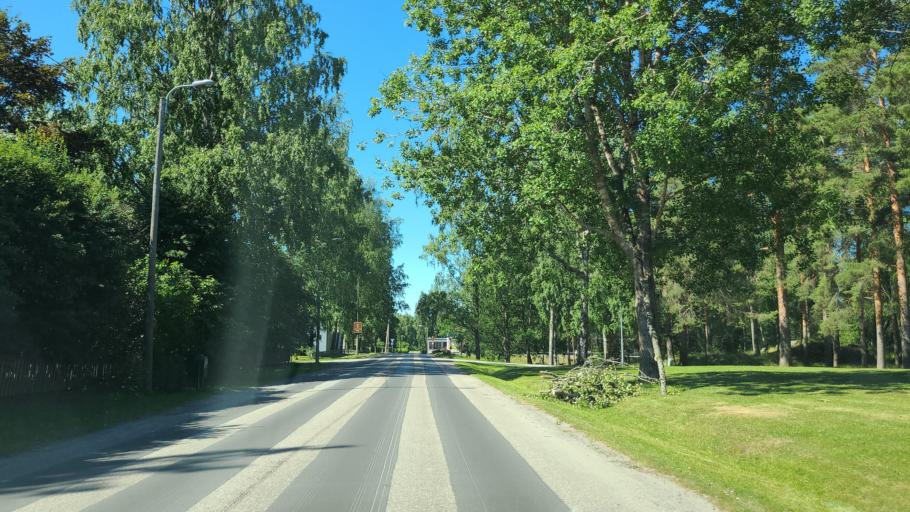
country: FI
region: Ostrobothnia
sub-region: Vaasa
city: Ristinummi
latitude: 63.0734
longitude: 21.7253
